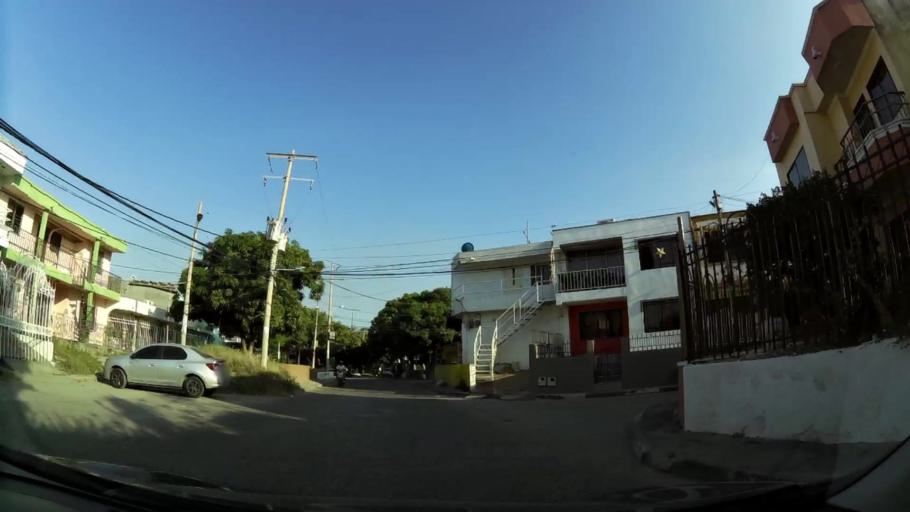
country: CO
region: Bolivar
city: Cartagena
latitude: 10.3813
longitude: -75.4804
